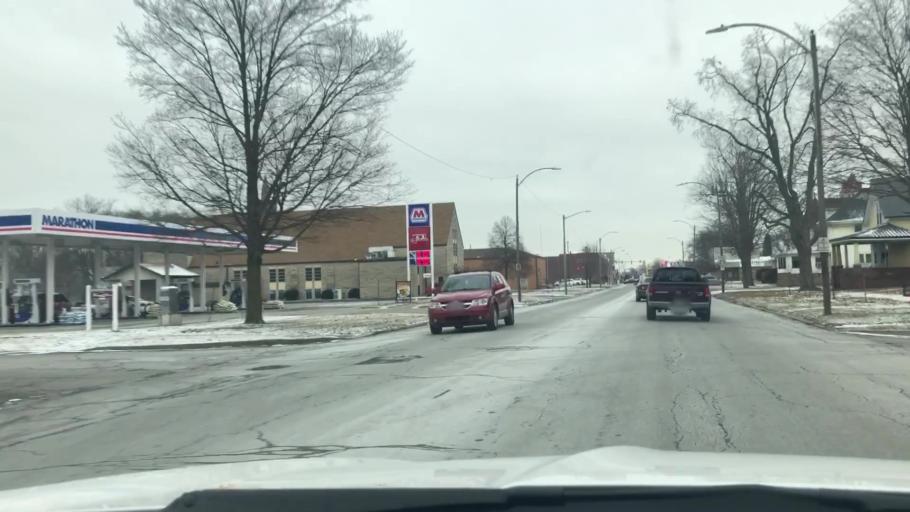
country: US
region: Indiana
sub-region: Fulton County
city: Rochester
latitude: 41.0627
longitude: -86.2162
